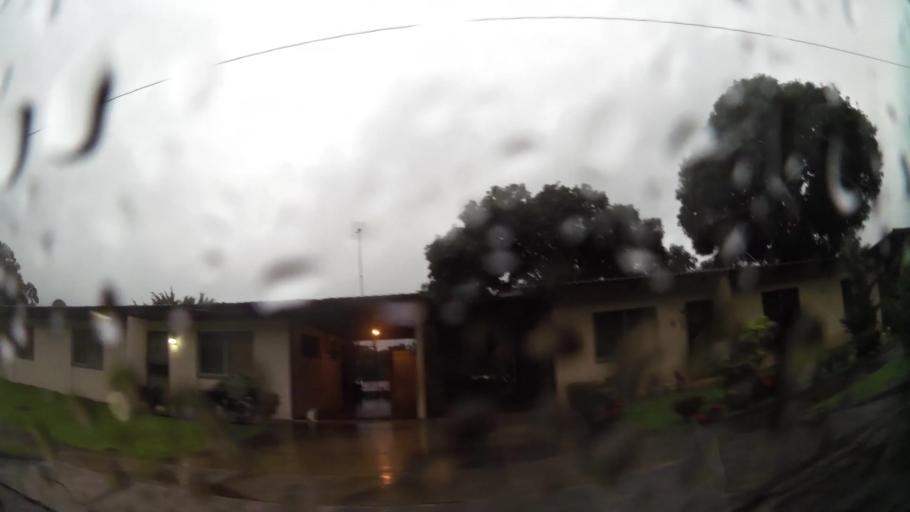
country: PA
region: Panama
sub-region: Distrito de Panama
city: Paraiso
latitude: 9.0210
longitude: -79.6123
